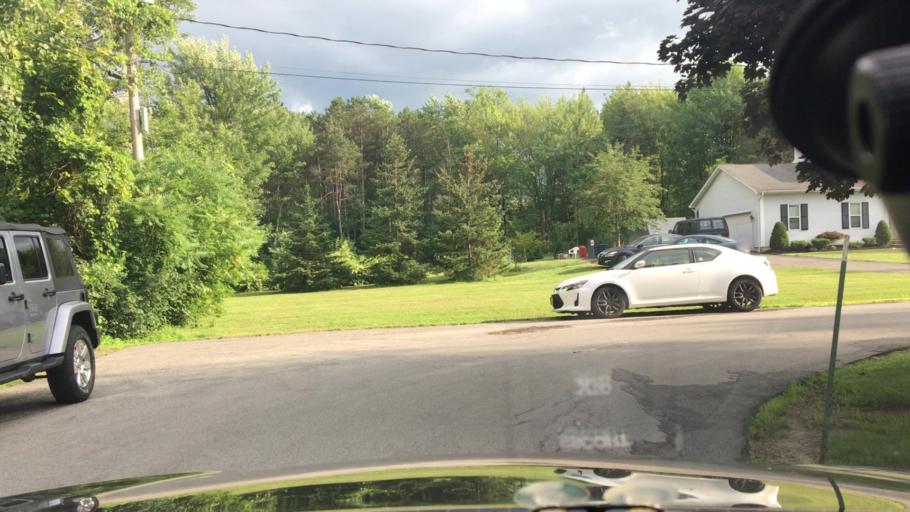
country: US
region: New York
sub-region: Erie County
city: Elma Center
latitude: 42.8186
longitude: -78.6588
